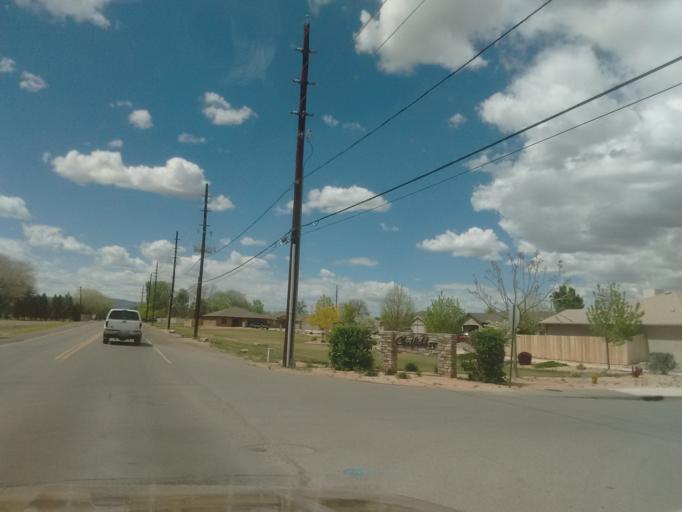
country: US
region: Colorado
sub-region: Mesa County
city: Clifton
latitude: 39.0773
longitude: -108.4663
